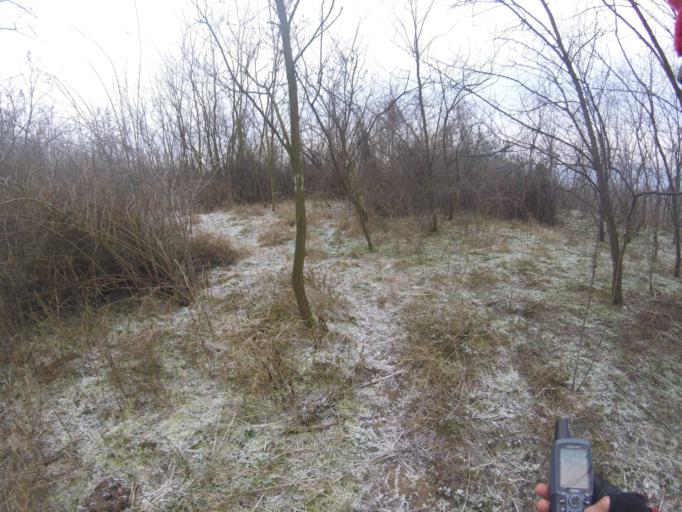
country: HU
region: Nograd
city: Paszto
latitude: 47.9385
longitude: 19.7068
